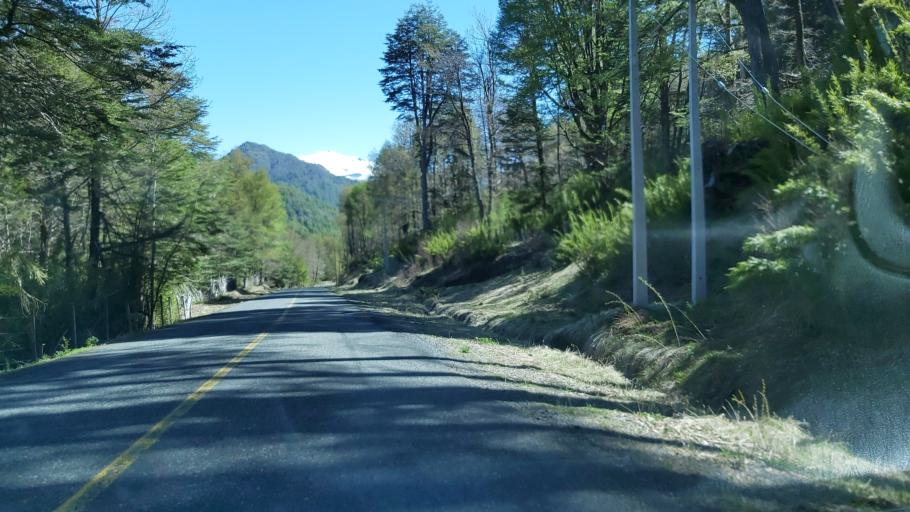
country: CL
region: Araucania
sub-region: Provincia de Cautin
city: Vilcun
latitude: -38.4632
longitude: -71.5177
